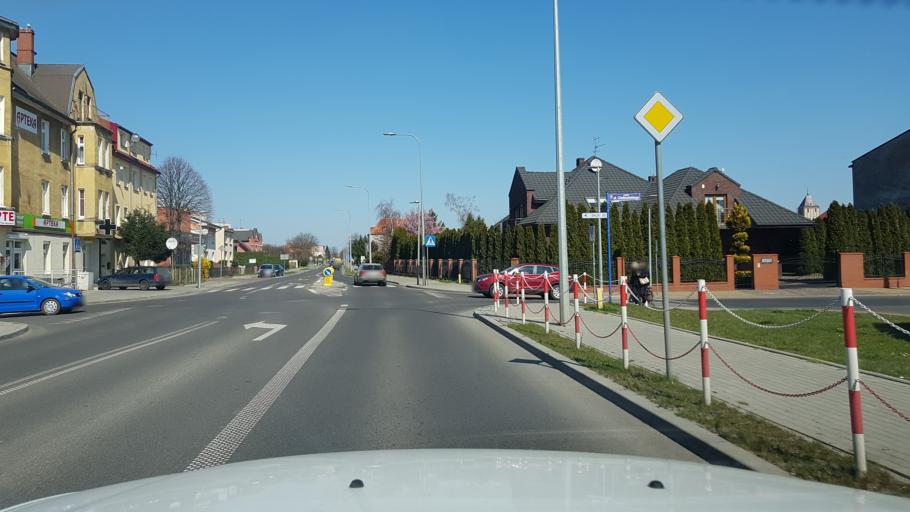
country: PL
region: West Pomeranian Voivodeship
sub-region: Powiat slawienski
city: Slawno
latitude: 54.3573
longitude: 16.6740
